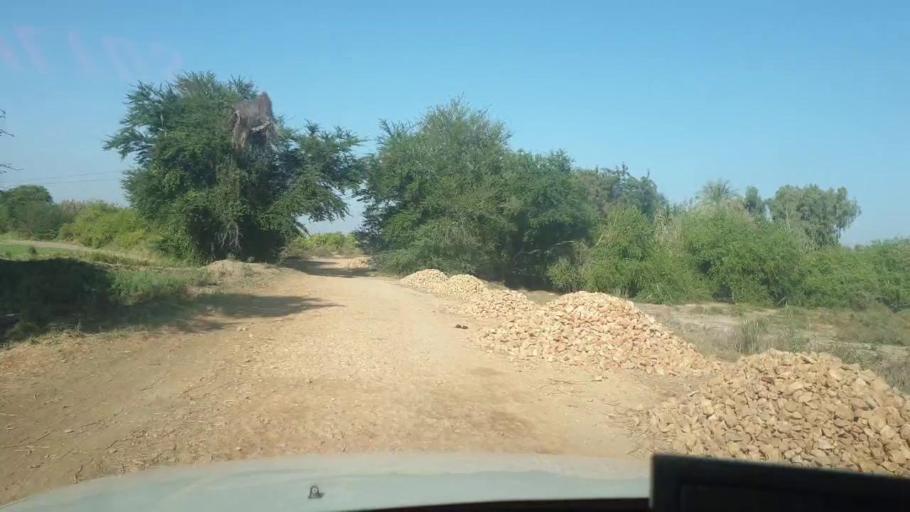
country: PK
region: Sindh
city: Mirpur Sakro
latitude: 24.5009
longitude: 67.6241
